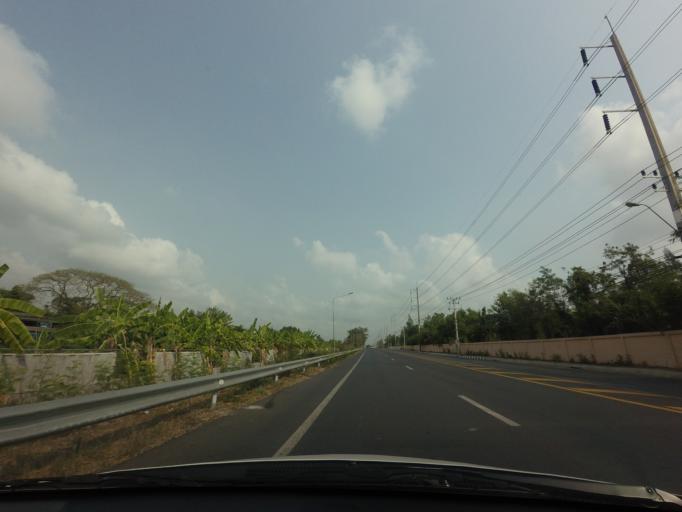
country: TH
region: Pathum Thani
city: Thanyaburi
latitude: 14.0173
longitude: 100.7102
